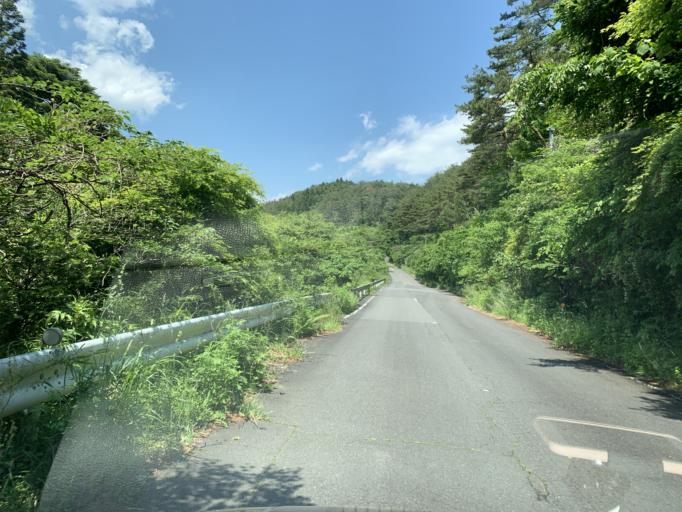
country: JP
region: Miyagi
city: Matsushima
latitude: 38.3543
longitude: 141.0575
